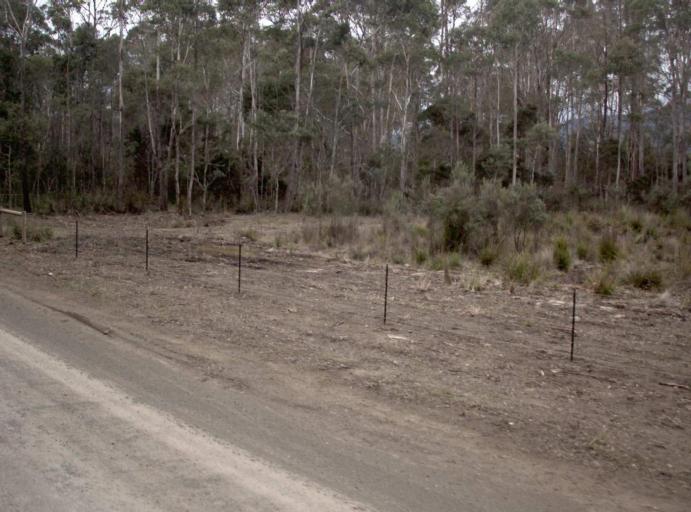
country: AU
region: Tasmania
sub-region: Launceston
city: Newstead
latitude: -41.3659
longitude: 147.2330
